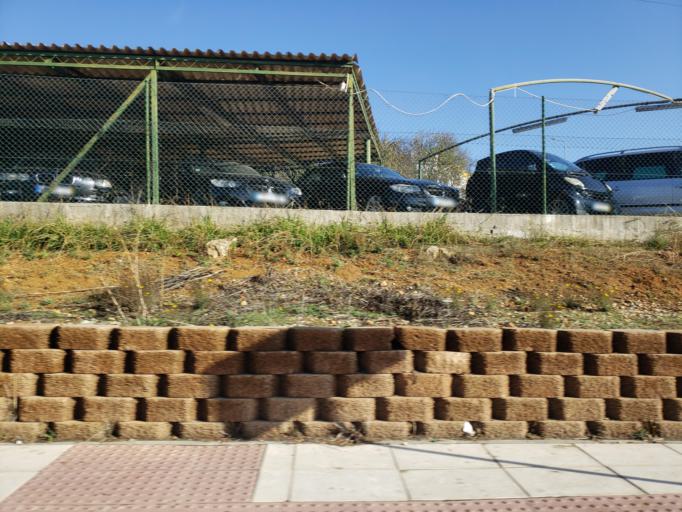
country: PT
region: Faro
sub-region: Portimao
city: Portimao
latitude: 37.1500
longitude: -8.5500
